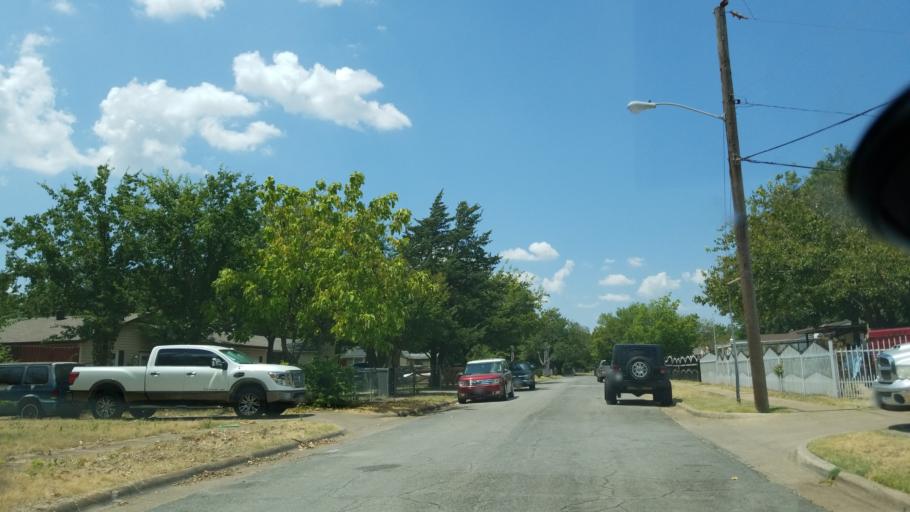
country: US
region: Texas
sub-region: Dallas County
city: Cockrell Hill
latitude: 32.7173
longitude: -96.8942
